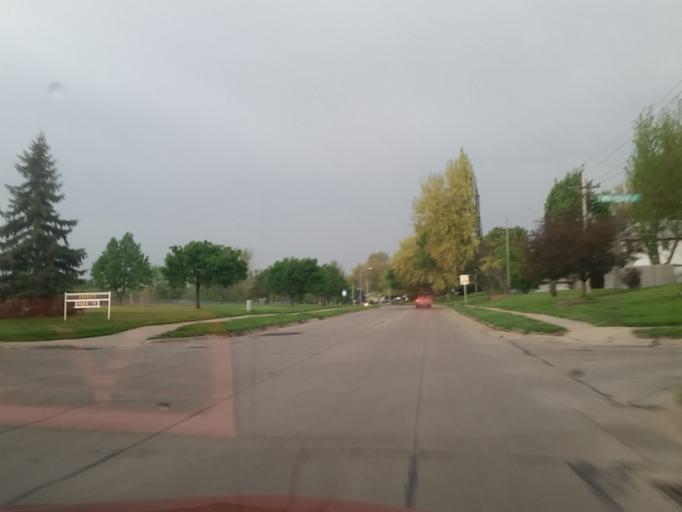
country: US
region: Nebraska
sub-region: Sarpy County
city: Offutt Air Force Base
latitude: 41.1469
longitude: -95.9201
